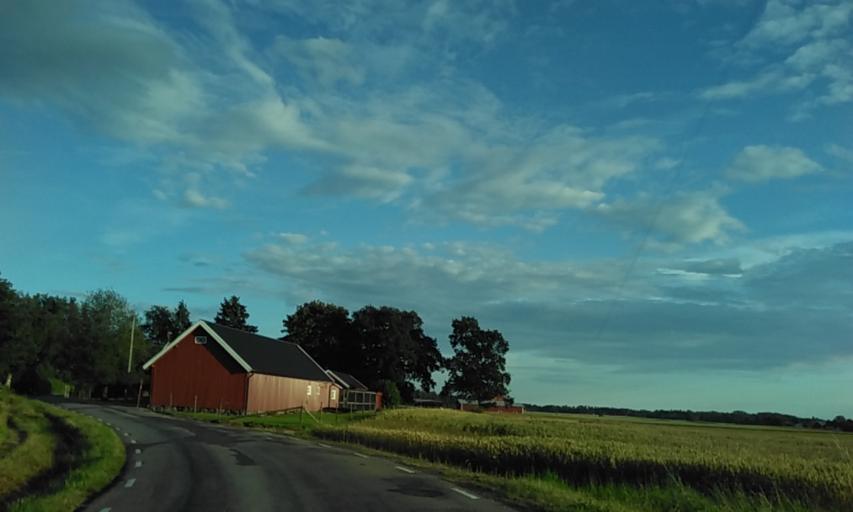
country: SE
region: Vaestra Goetaland
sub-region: Grastorps Kommun
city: Graestorp
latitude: 58.3409
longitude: 12.7607
